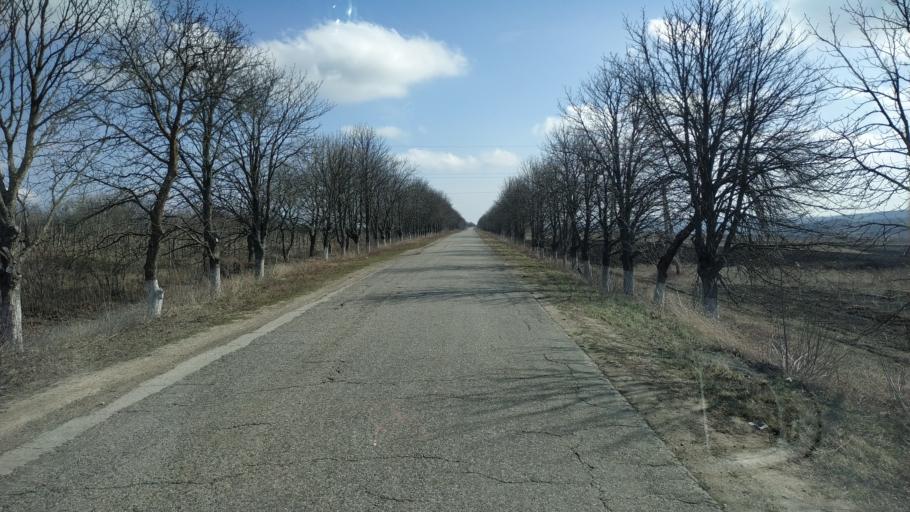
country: MD
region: Hincesti
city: Hincesti
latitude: 46.8556
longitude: 28.6393
